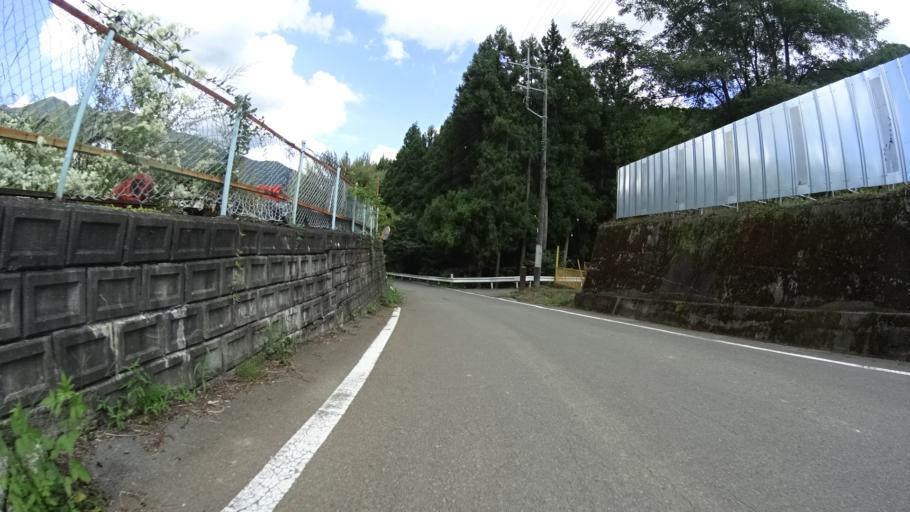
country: JP
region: Yamanashi
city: Enzan
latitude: 35.5992
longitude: 138.7999
